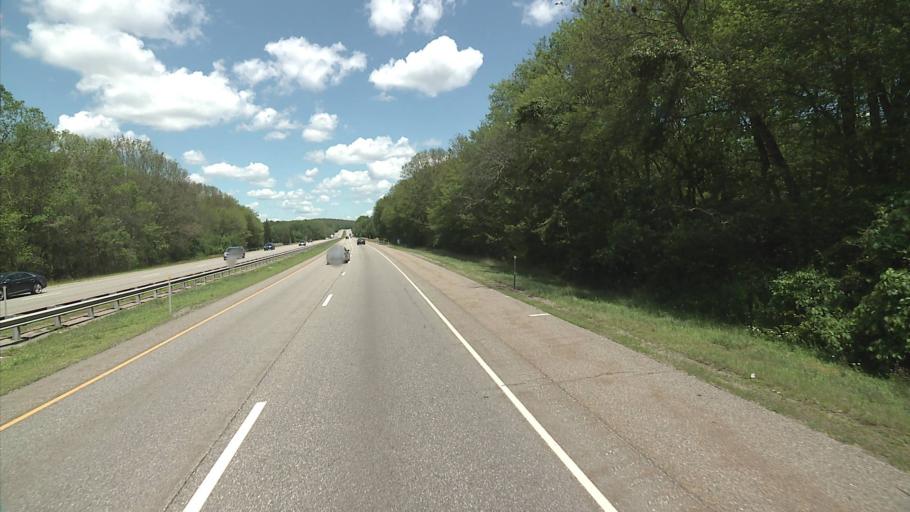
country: US
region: Connecticut
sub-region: Windham County
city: Plainfield
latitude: 41.6739
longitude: -71.9089
